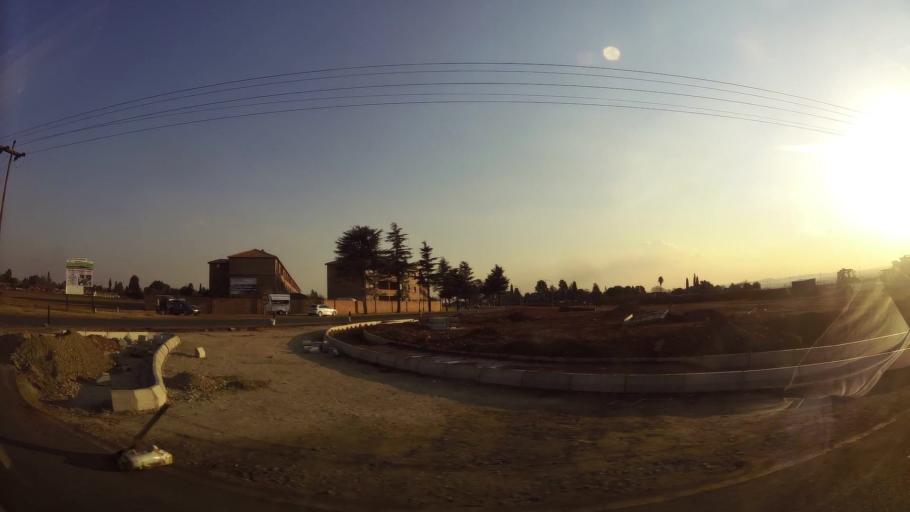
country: ZA
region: Gauteng
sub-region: Ekurhuleni Metropolitan Municipality
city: Boksburg
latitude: -26.2953
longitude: 28.2528
